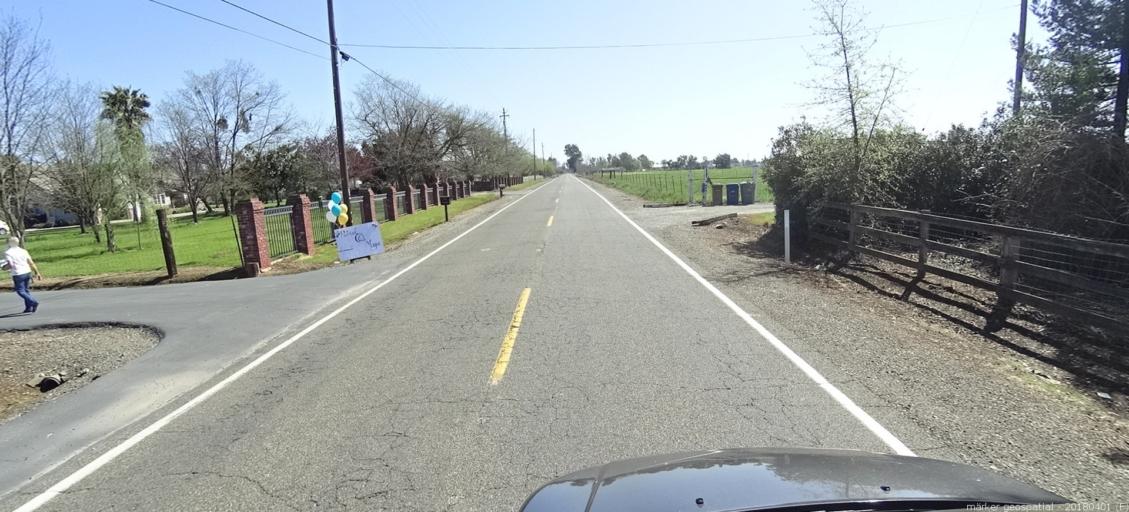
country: US
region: California
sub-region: Sacramento County
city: Wilton
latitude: 38.4086
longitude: -121.2335
